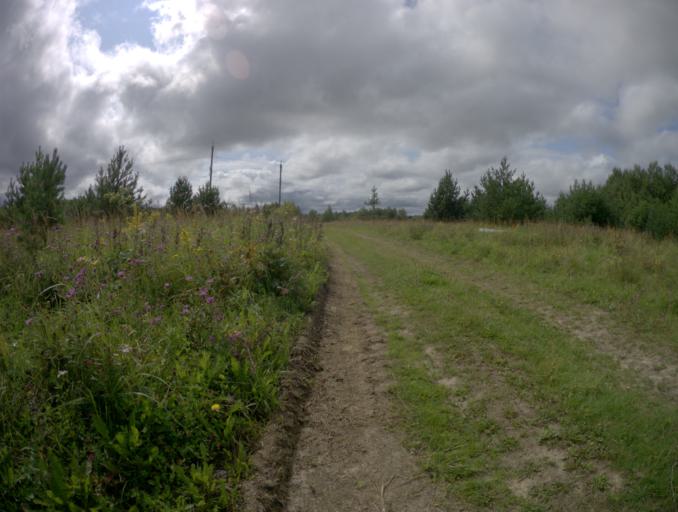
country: RU
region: Vladimir
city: Raduzhnyy
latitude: 56.0148
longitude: 40.3361
